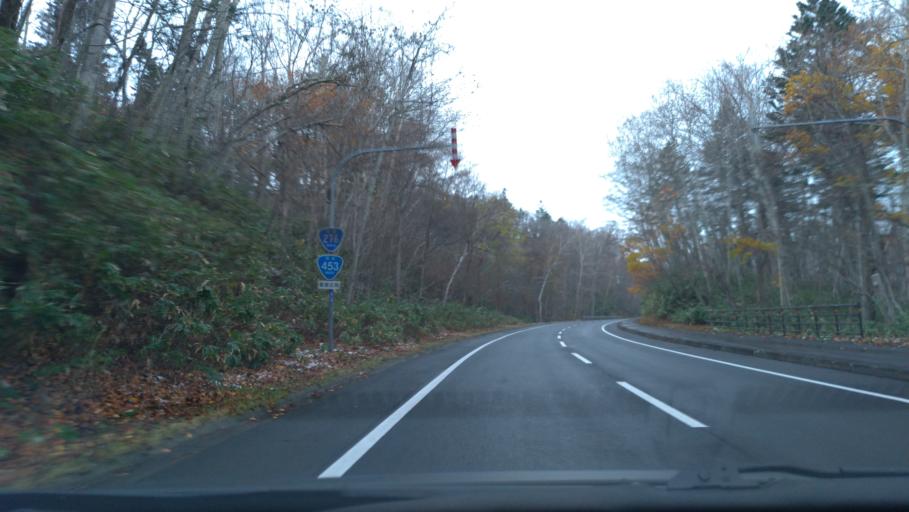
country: JP
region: Hokkaido
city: Shiraoi
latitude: 42.7353
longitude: 141.3668
